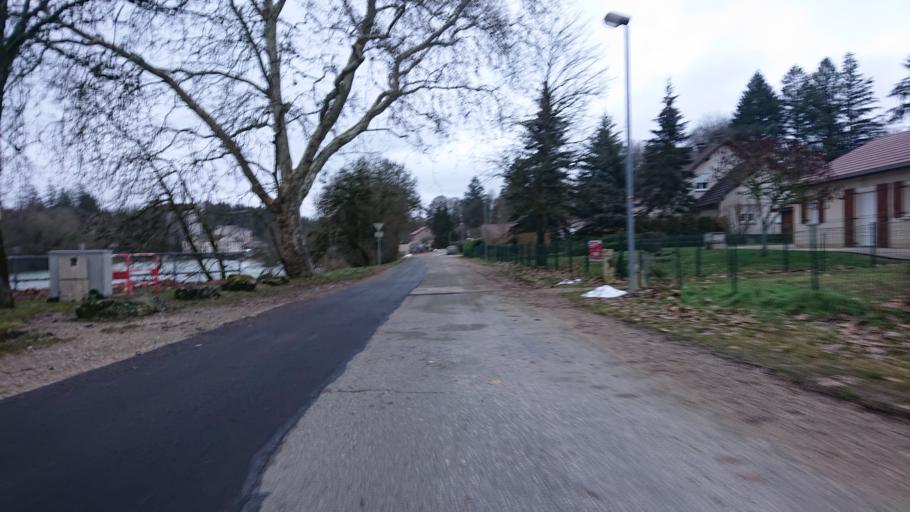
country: FR
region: Franche-Comte
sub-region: Departement du Jura
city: Clairvaux-les-Lacs
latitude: 46.5840
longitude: 5.7002
